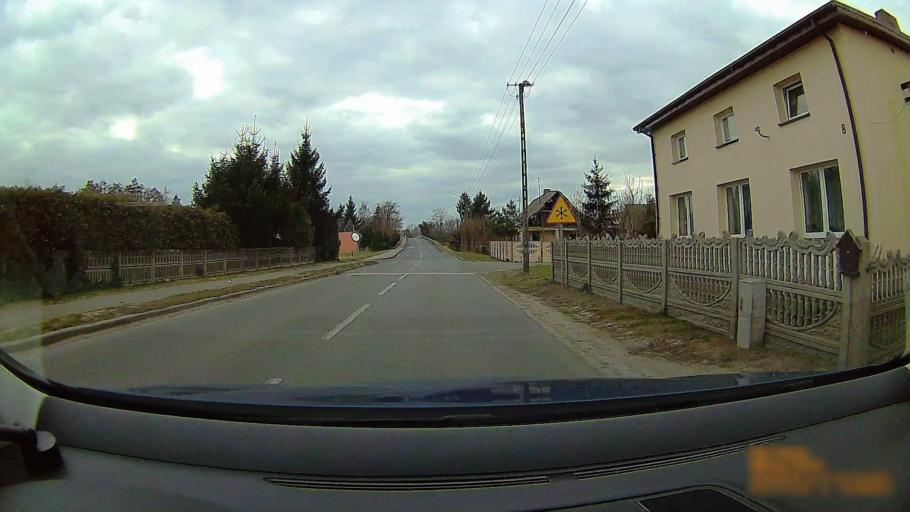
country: PL
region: Greater Poland Voivodeship
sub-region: Powiat koninski
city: Golina
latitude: 52.1842
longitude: 18.1067
